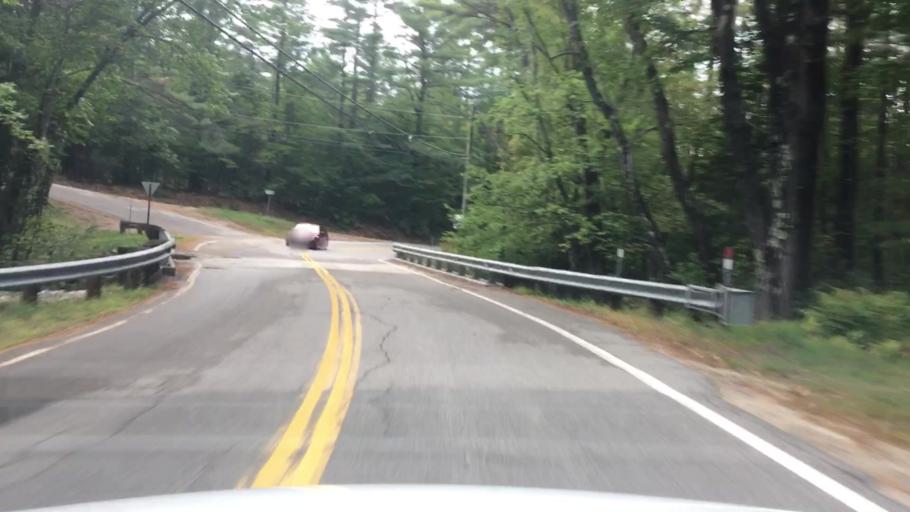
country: US
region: New Hampshire
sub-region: Carroll County
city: Effingham
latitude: 43.7295
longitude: -71.0023
